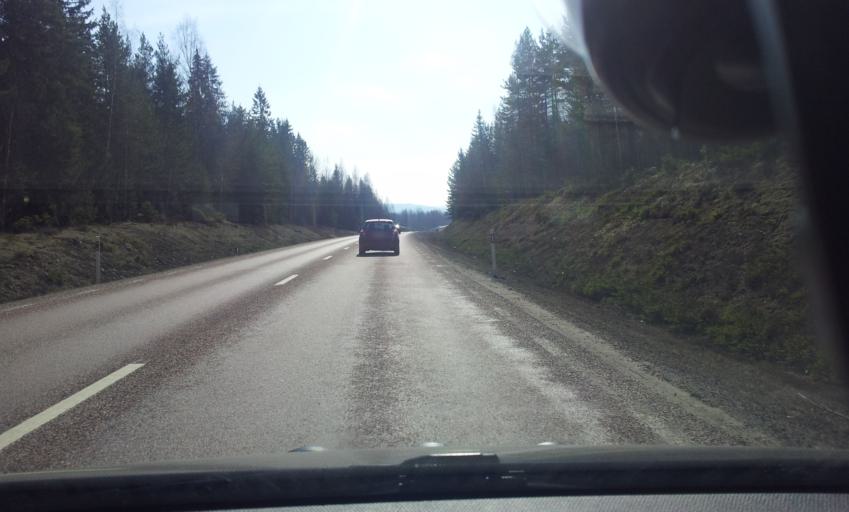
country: SE
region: Gaevleborg
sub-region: Ljusdals Kommun
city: Jaervsoe
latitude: 61.7701
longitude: 16.1555
